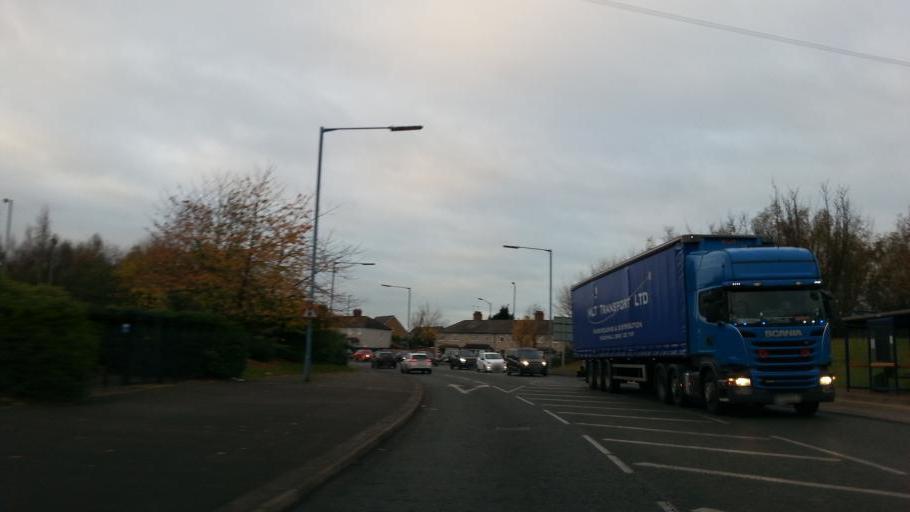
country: GB
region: England
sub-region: Sandwell
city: Wednesbury
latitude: 52.5478
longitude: -2.0310
